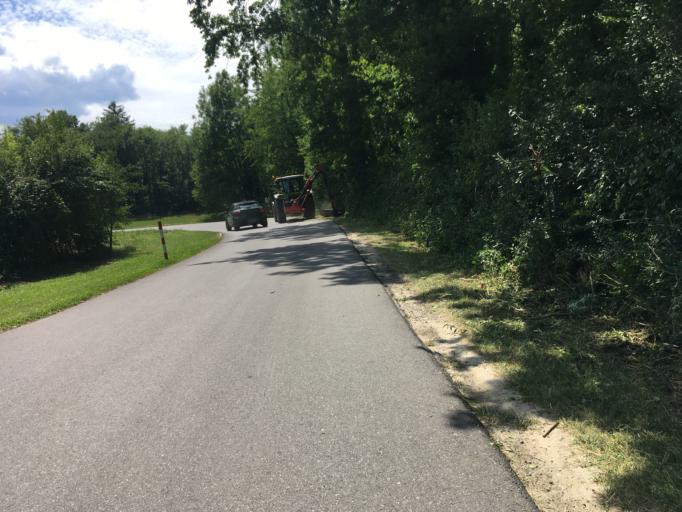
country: CH
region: Vaud
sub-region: Broye-Vully District
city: Payerne
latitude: 46.9025
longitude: 6.9276
